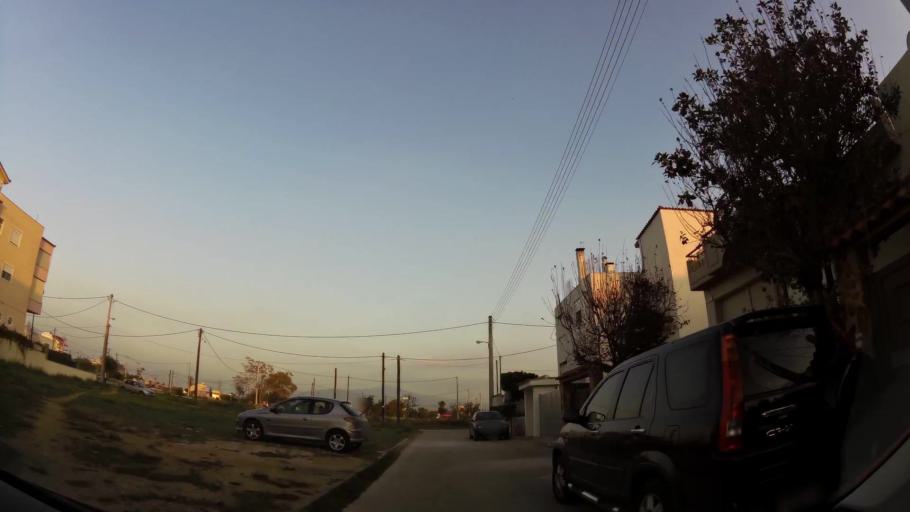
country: GR
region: Attica
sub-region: Nomarchia Anatolikis Attikis
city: Acharnes
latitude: 38.0898
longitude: 23.7465
